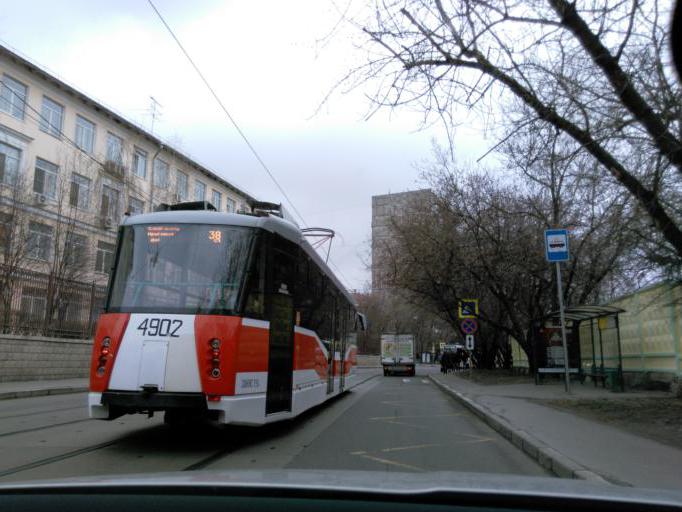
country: RU
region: Moscow
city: Zamoskvorech'ye
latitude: 55.7154
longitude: 37.6333
